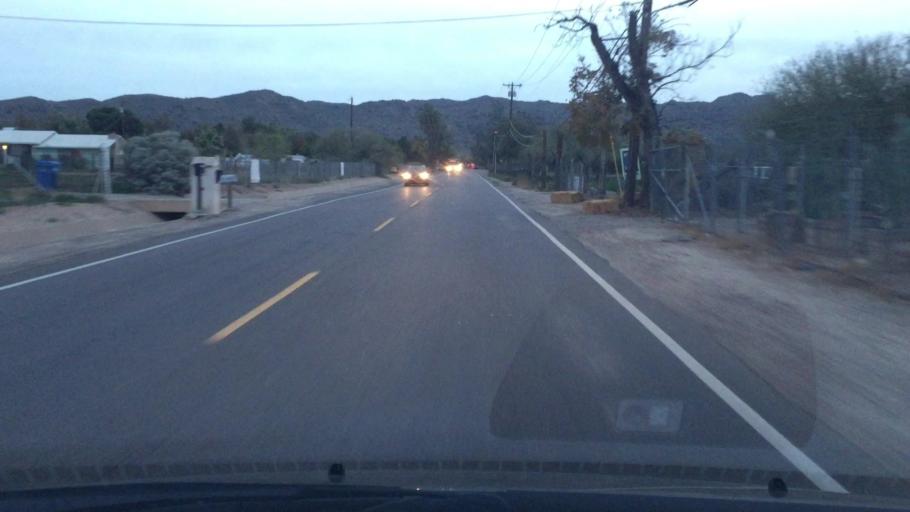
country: US
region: Arizona
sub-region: Maricopa County
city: Guadalupe
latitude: 33.3882
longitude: -112.0126
